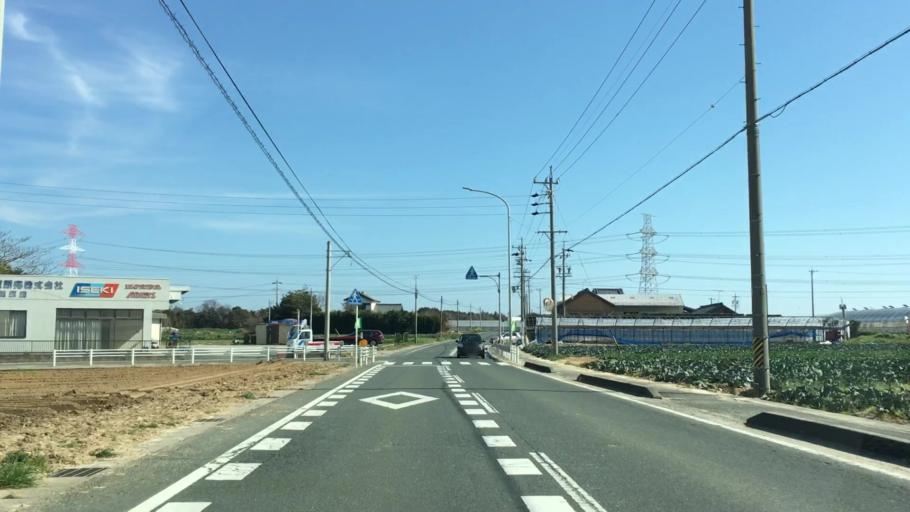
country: JP
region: Aichi
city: Tahara
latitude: 34.6565
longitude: 137.2870
